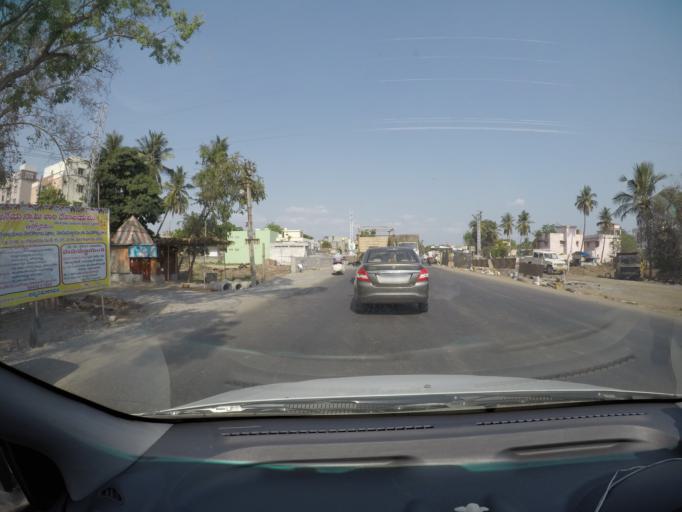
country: IN
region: Andhra Pradesh
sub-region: Krishna
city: Yanamalakuduru
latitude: 16.4756
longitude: 80.7086
